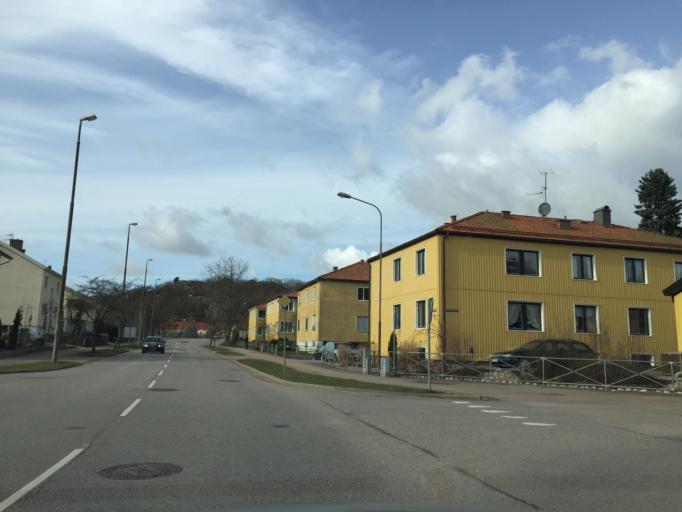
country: SE
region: Vaestra Goetaland
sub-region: Uddevalla Kommun
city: Uddevalla
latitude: 58.3551
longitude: 11.9449
